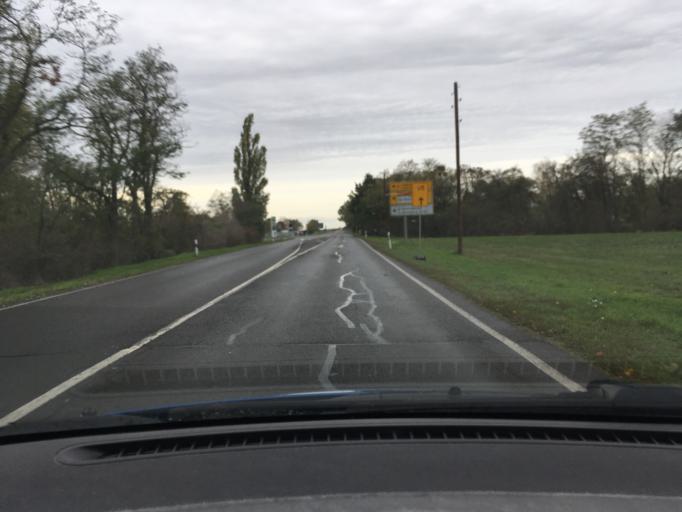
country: DE
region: Saxony-Anhalt
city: Zerbst
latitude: 51.9767
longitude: 12.0632
